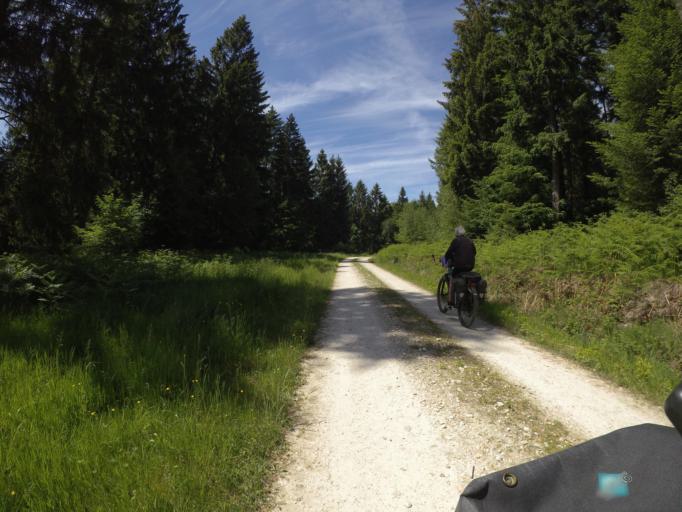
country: DE
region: Rheinland-Pfalz
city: Morbach
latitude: 49.7742
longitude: 7.1112
